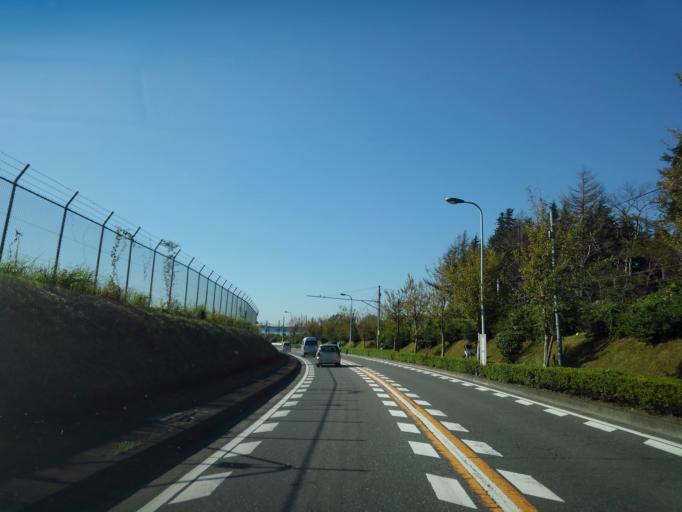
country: JP
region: Tokyo
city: Fussa
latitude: 35.7672
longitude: 139.3427
